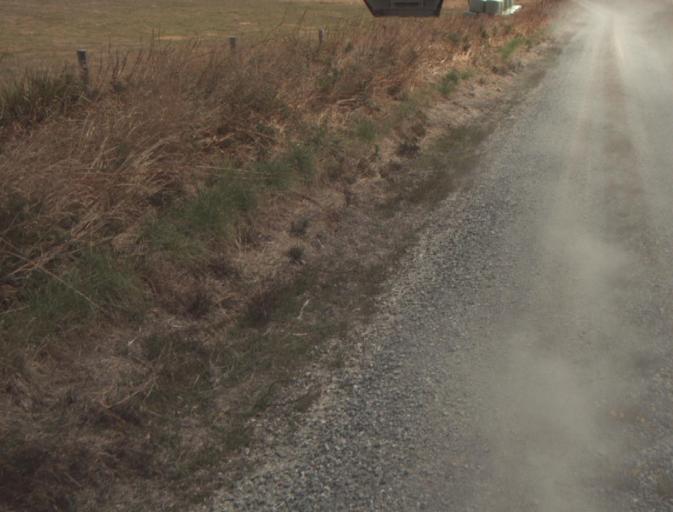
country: AU
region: Tasmania
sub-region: Launceston
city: Mayfield
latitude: -41.2147
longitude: 147.1075
